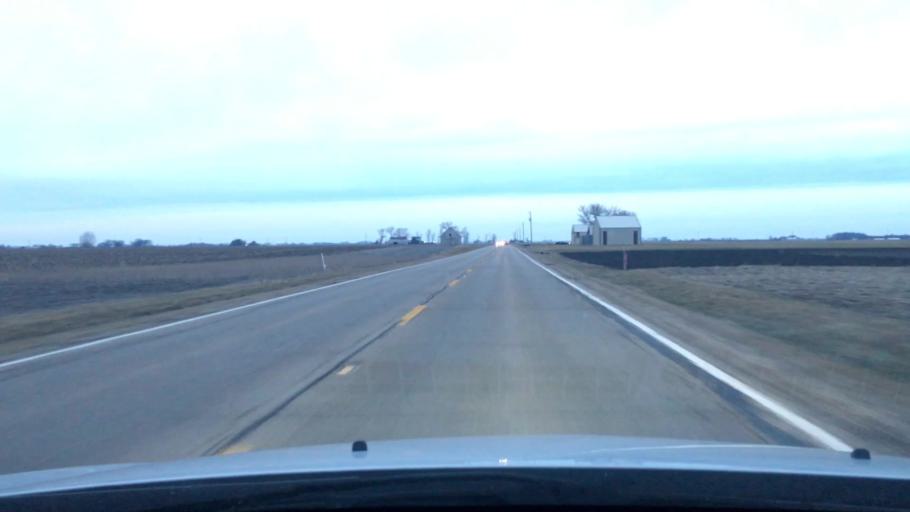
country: US
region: Illinois
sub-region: LaSalle County
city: Peru
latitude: 41.4179
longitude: -89.1263
